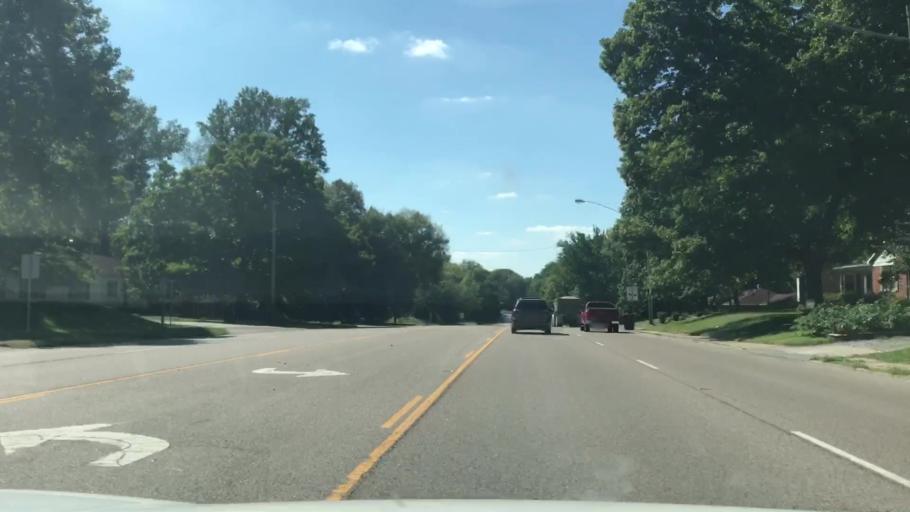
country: US
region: Illinois
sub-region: Saint Clair County
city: Swansea
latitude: 38.5419
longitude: -90.0406
